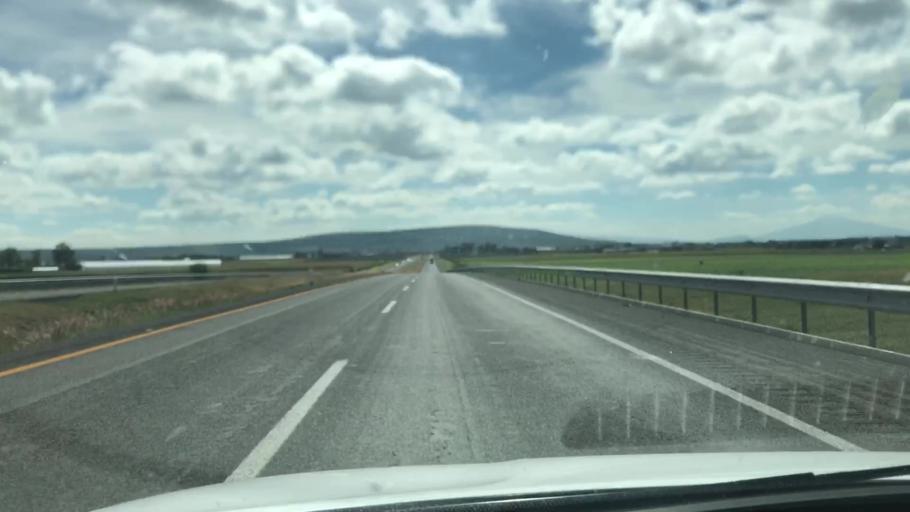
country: MX
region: Guanajuato
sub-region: Salamanca
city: El Recuerdo de Ancon (Xoconoxtle de Arriba)
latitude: 20.6514
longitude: -101.1833
